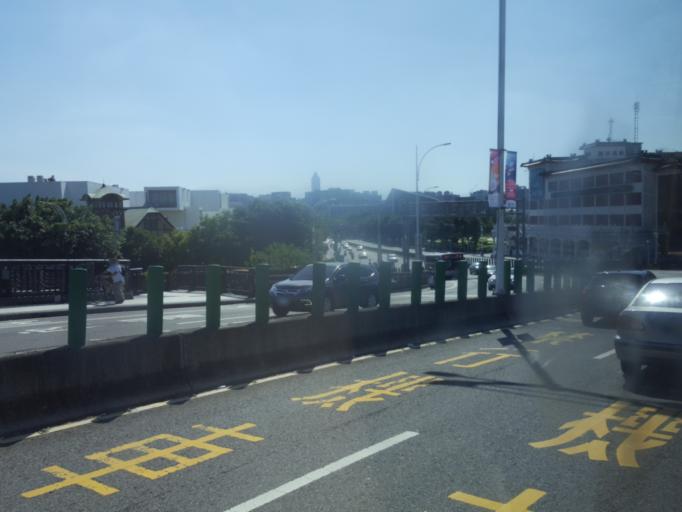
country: TW
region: Taipei
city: Taipei
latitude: 25.0740
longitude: 121.5247
